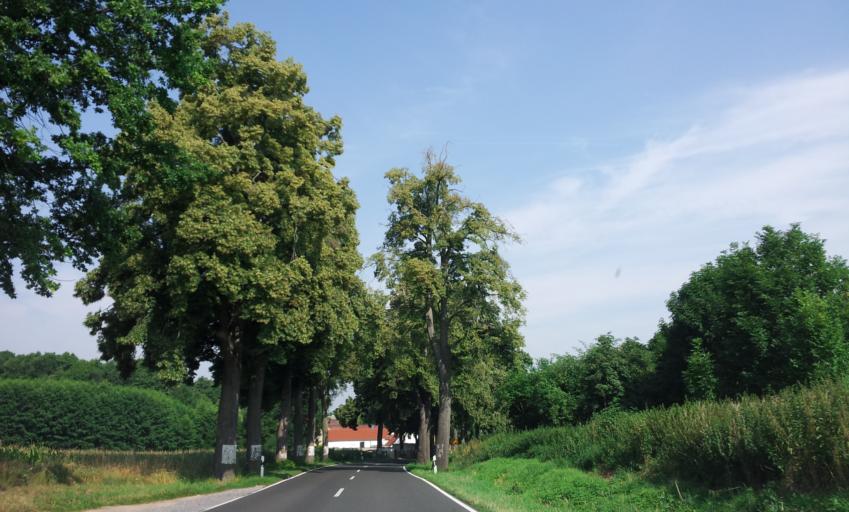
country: DE
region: Brandenburg
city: Treuenbrietzen
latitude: 52.1117
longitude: 12.8224
